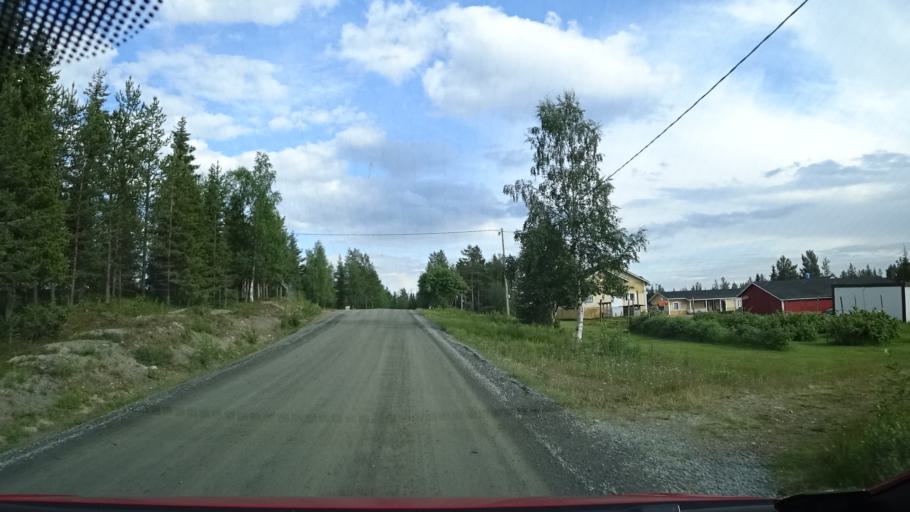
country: FI
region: Lapland
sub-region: Tunturi-Lappi
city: Kittilae
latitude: 67.9067
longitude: 25.0792
